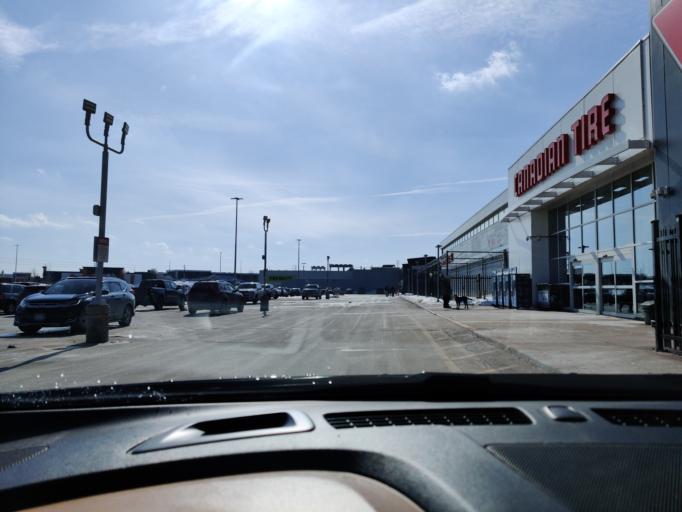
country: CA
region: Ontario
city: Collingwood
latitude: 44.5048
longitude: -80.2370
